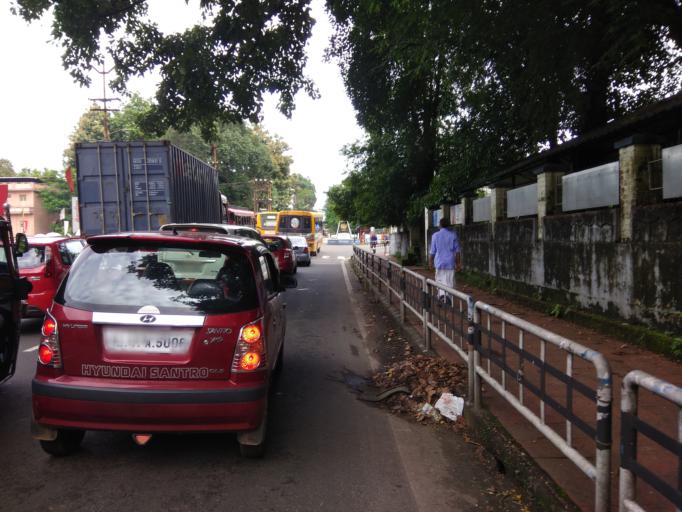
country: IN
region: Kerala
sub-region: Thrissur District
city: Trichur
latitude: 10.5315
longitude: 76.2194
